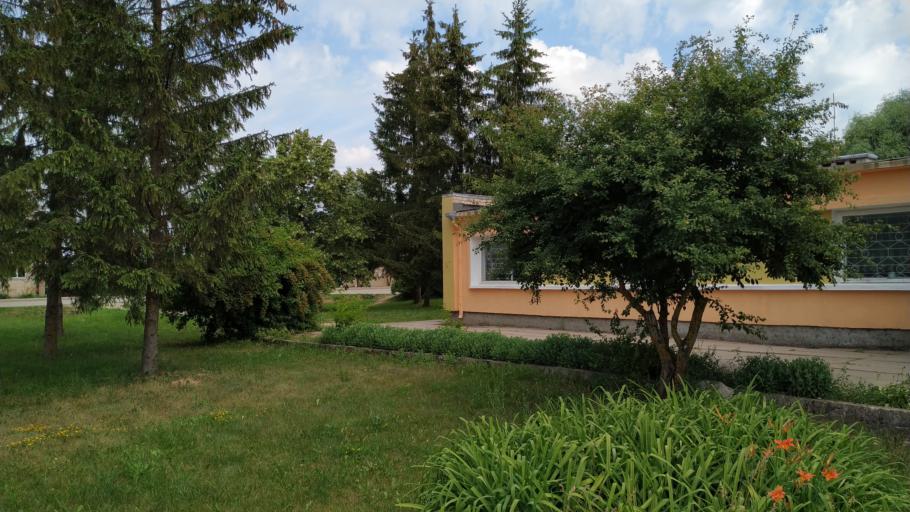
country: LT
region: Panevezys
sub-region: Birzai
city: Birzai
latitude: 56.2633
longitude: 24.6104
